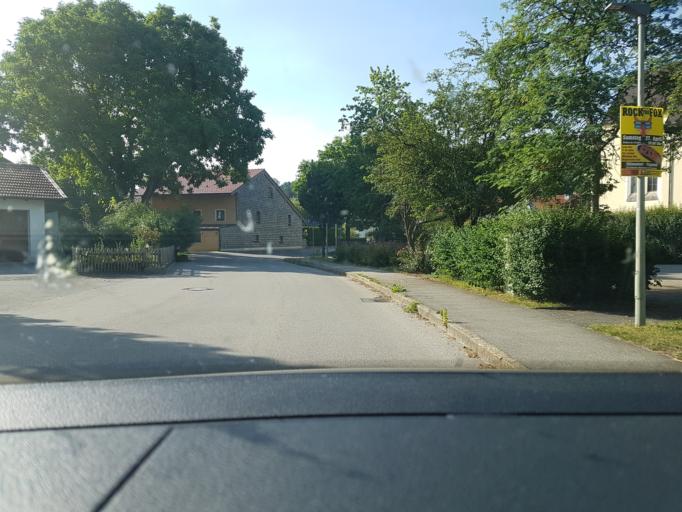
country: DE
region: Bavaria
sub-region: Upper Bavaria
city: Teisendorf
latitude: 47.8512
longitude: 12.7852
